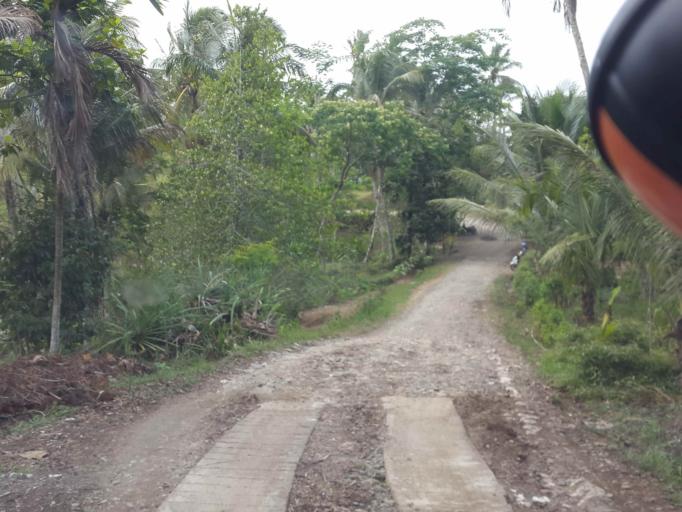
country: ID
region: East Java
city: Krajan
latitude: -8.2343
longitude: 111.1331
